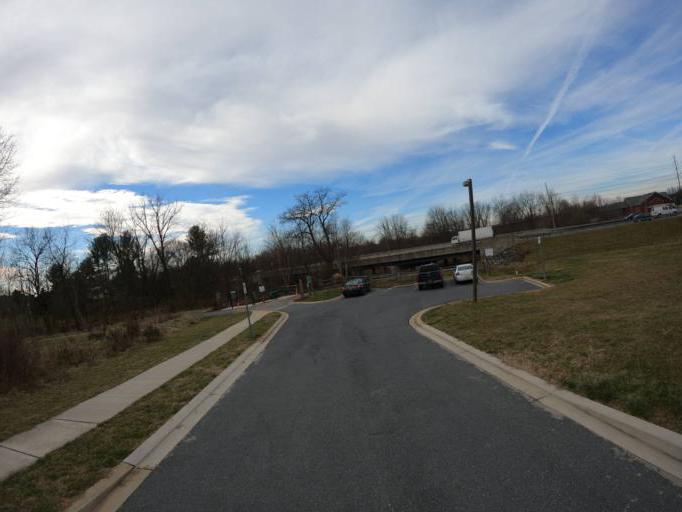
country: US
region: Maryland
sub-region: Frederick County
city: Ballenger Creek
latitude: 39.3777
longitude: -77.4213
